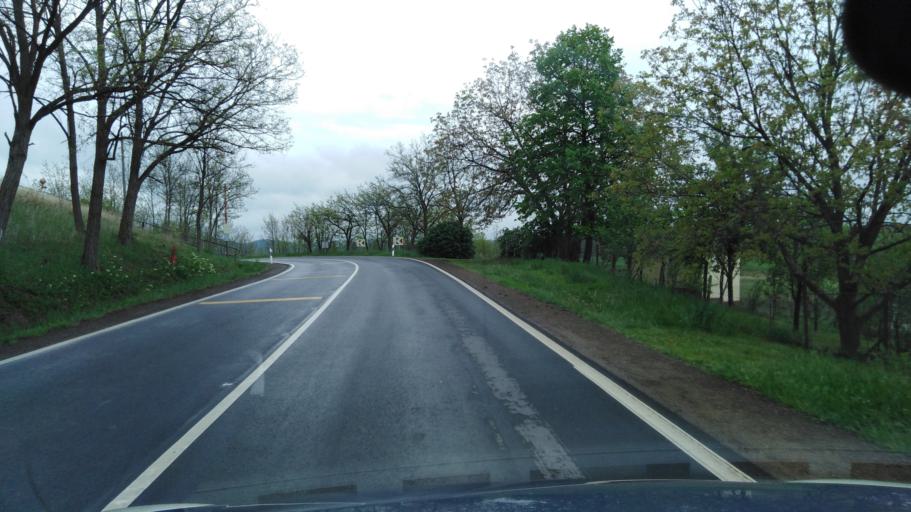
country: HU
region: Nograd
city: Karancskeszi
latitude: 48.1201
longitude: 19.6426
